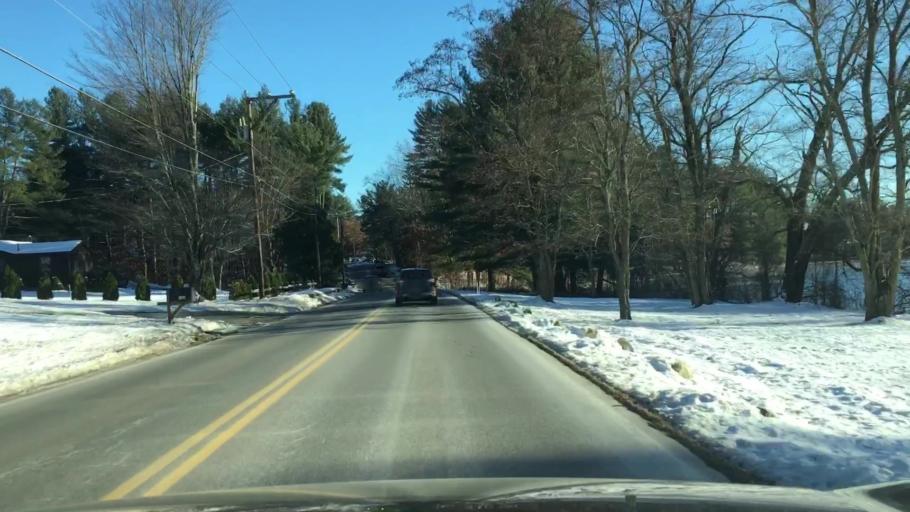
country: US
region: New Hampshire
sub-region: Hillsborough County
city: Hollis
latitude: 42.8080
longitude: -71.5583
